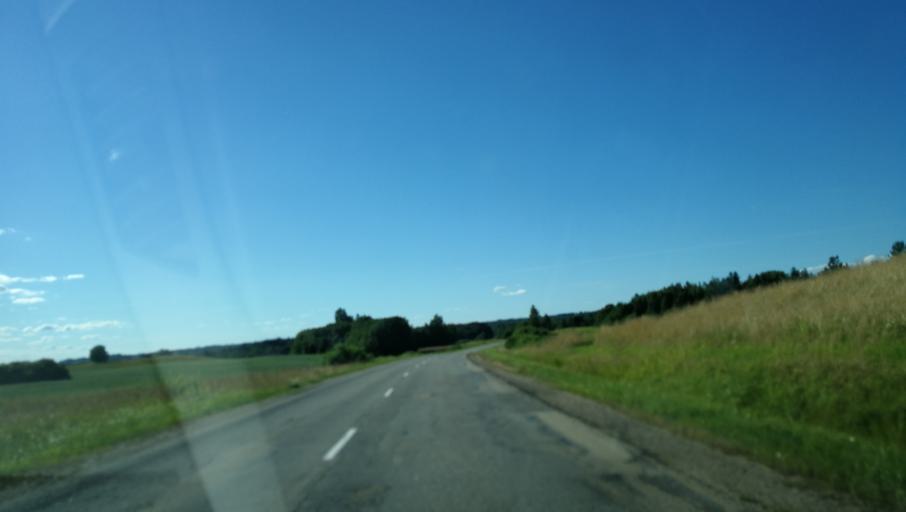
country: LV
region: Jaunpiebalga
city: Jaunpiebalga
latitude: 56.9864
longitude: 26.0189
